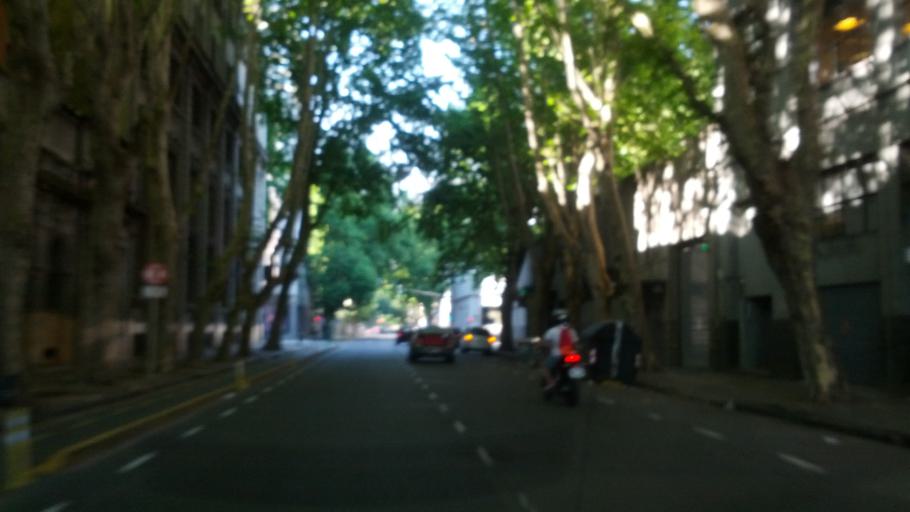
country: AR
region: Buenos Aires F.D.
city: Buenos Aires
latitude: -34.6215
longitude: -58.3668
